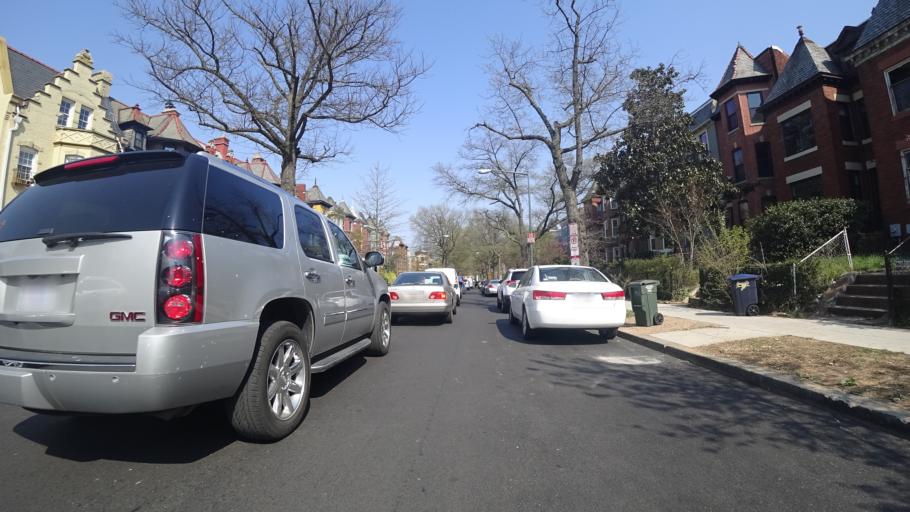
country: US
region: Washington, D.C.
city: Washington, D.C.
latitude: 38.9268
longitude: -77.0312
